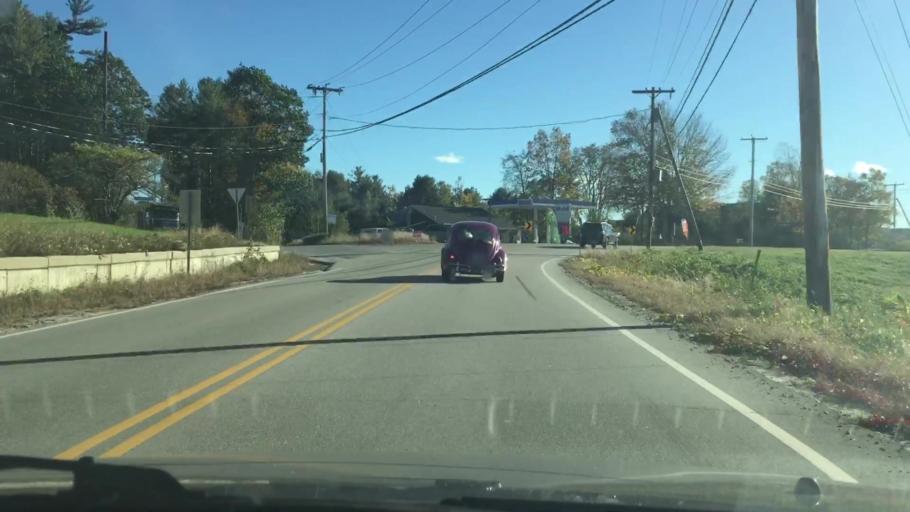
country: US
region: New Hampshire
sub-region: Cheshire County
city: Swanzey
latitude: 42.8796
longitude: -72.2703
